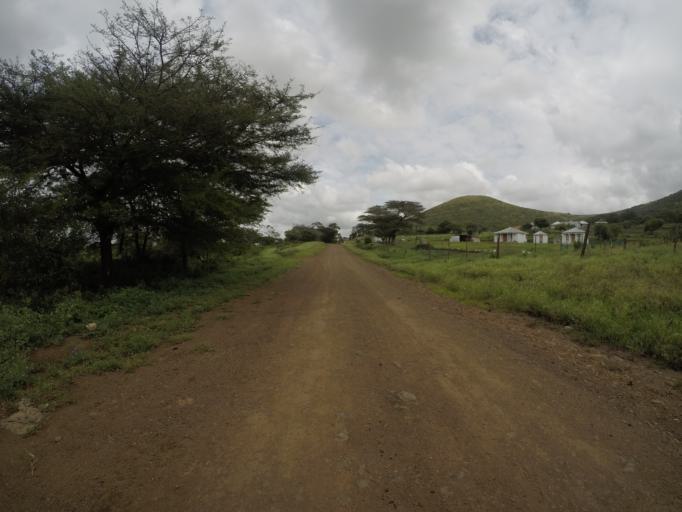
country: ZA
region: KwaZulu-Natal
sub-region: uThungulu District Municipality
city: Empangeni
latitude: -28.5918
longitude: 31.8870
